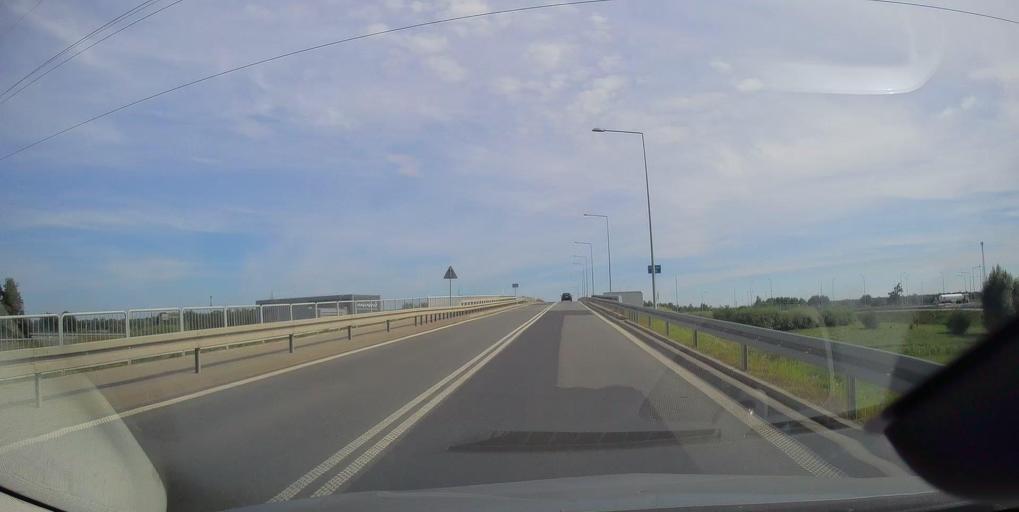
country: PL
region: Lodz Voivodeship
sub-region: Powiat tomaszowski
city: Tomaszow Mazowiecki
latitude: 51.5515
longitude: 19.9879
